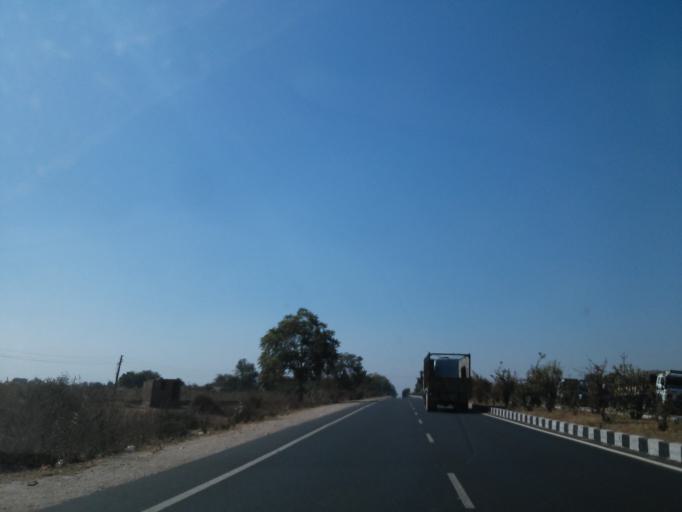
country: IN
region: Gujarat
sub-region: Sabar Kantha
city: Modasa
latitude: 23.6727
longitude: 73.3410
